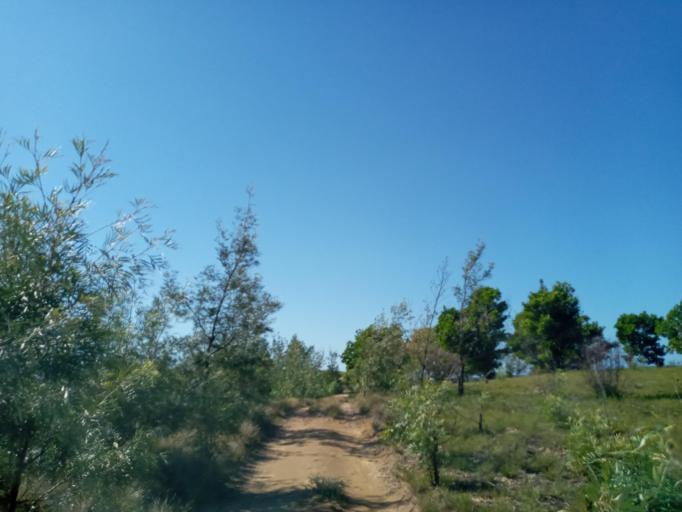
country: MG
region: Anosy
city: Fort Dauphin
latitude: -24.9112
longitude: 47.0898
